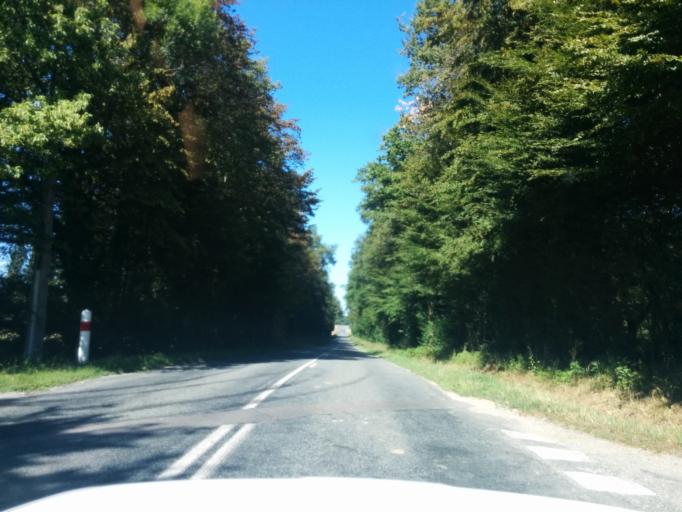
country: FR
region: Rhone-Alpes
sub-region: Departement de l'Ain
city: Chalamont
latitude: 45.9557
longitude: 5.1453
